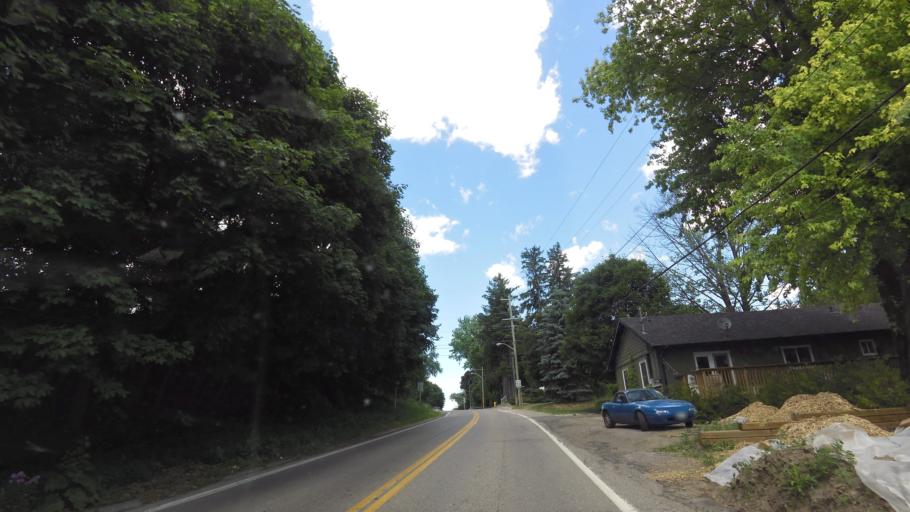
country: CA
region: Ontario
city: Oshawa
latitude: 43.9699
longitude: -78.6141
